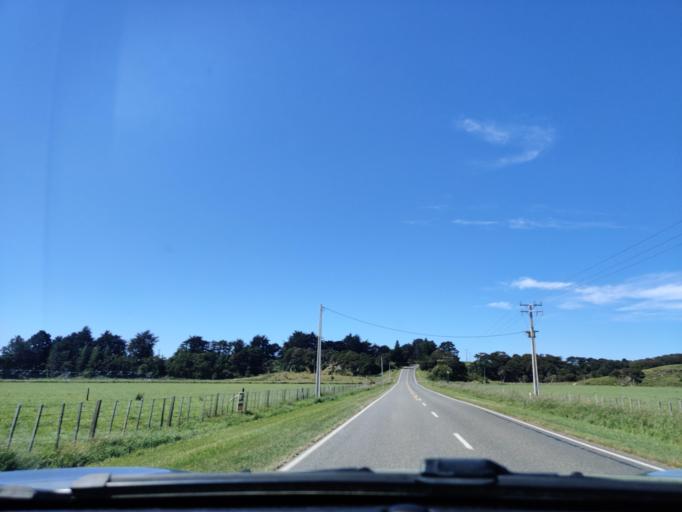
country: NZ
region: Wellington
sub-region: South Wairarapa District
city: Waipawa
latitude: -41.3149
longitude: 175.2609
